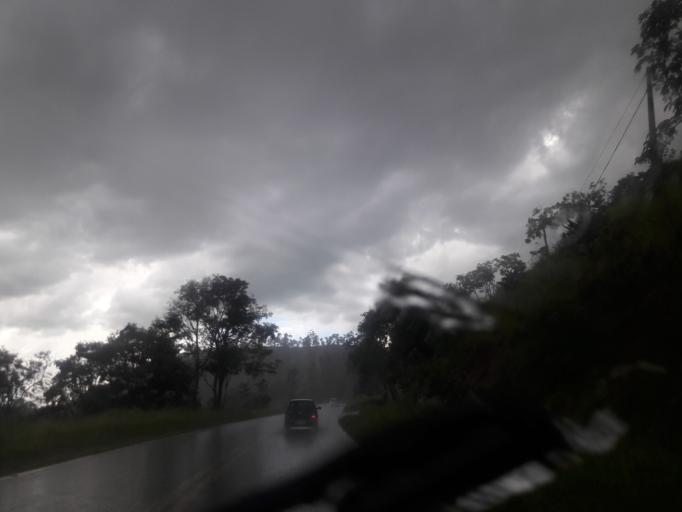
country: BR
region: Sao Paulo
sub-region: Bom Jesus Dos Perdoes
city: Bom Jesus dos Perdoes
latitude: -23.1919
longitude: -46.3978
